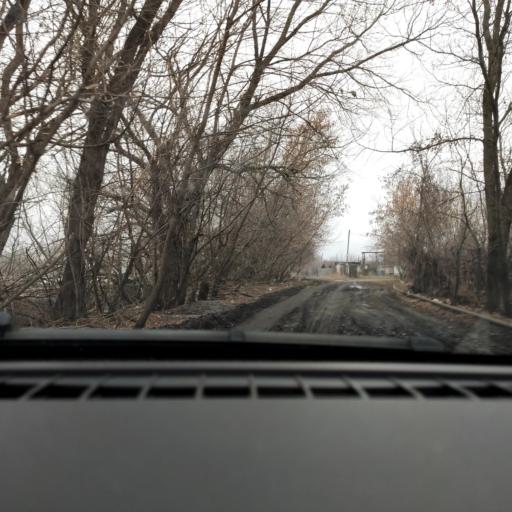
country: RU
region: Voronezj
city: Maslovka
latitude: 51.6093
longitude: 39.2723
